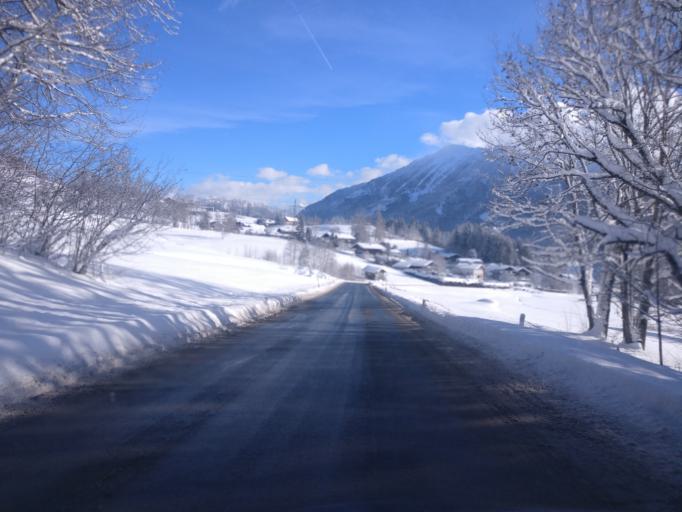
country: AT
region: Salzburg
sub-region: Politischer Bezirk Sankt Johann im Pongau
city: Goldegg
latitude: 47.3232
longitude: 13.0975
